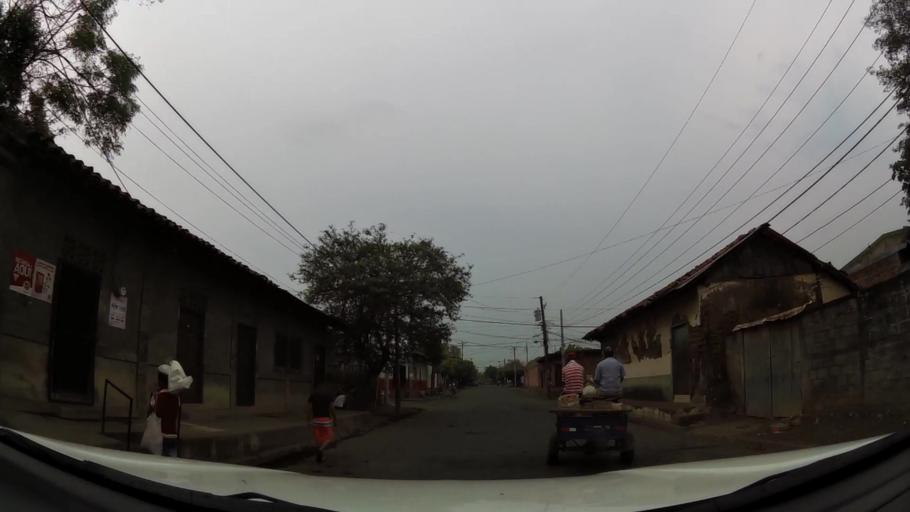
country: NI
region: Leon
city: Leon
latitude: 12.4254
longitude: -86.8797
